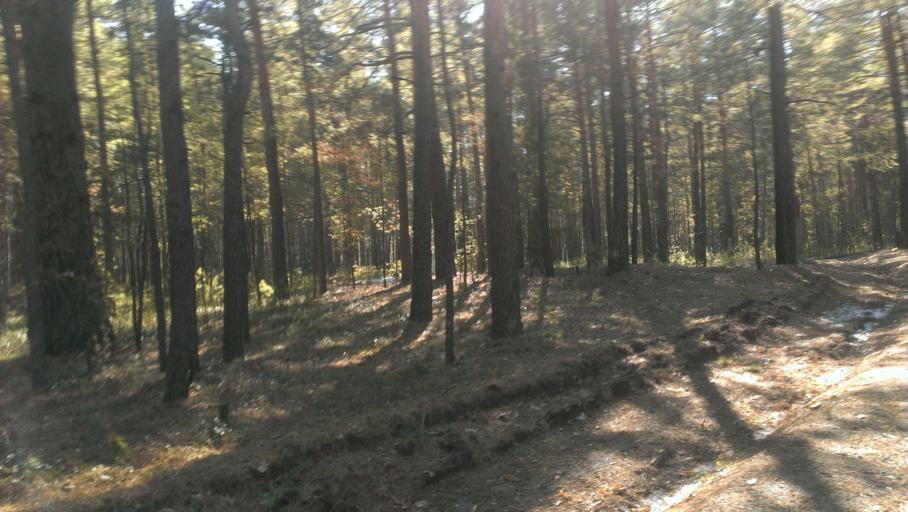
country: RU
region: Altai Krai
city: Yuzhnyy
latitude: 53.2978
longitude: 83.6976
